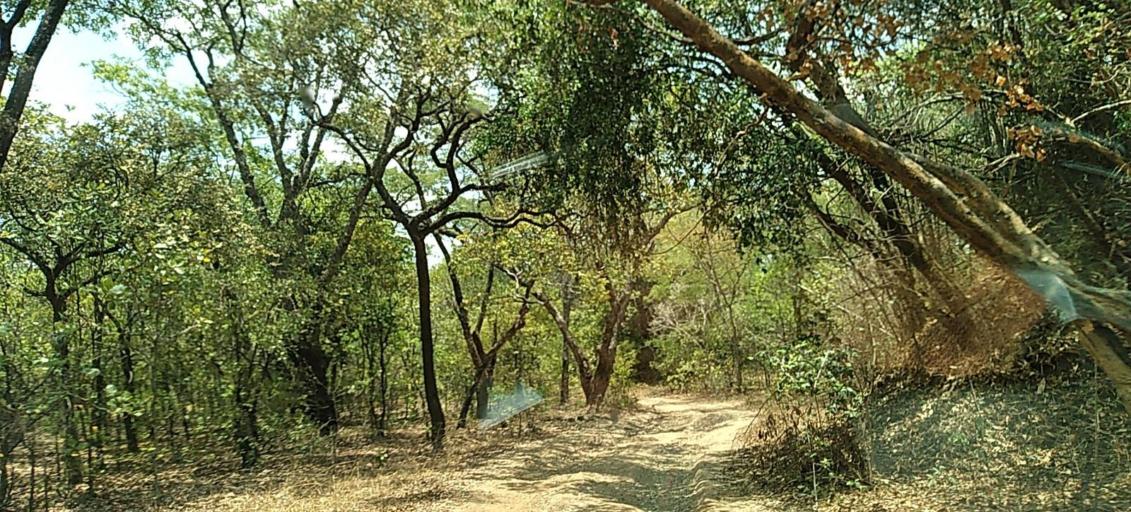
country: ZM
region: Copperbelt
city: Chililabombwe
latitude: -12.4647
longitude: 27.6992
